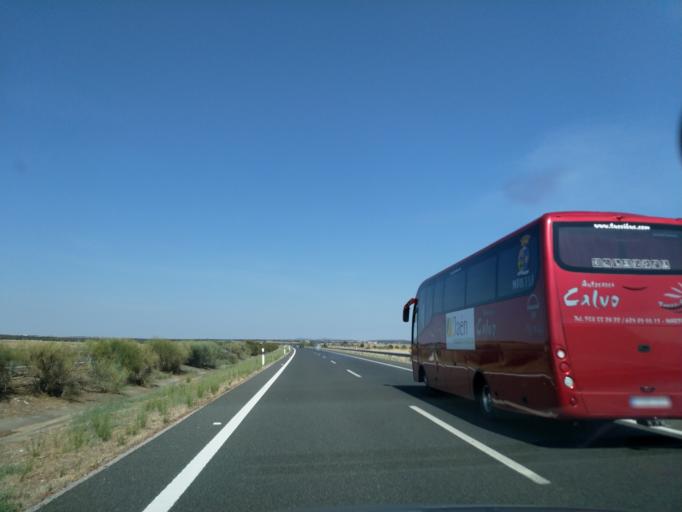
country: ES
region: Extremadura
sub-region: Provincia de Caceres
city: Casas de Don Antonio
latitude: 39.2479
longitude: -6.3067
